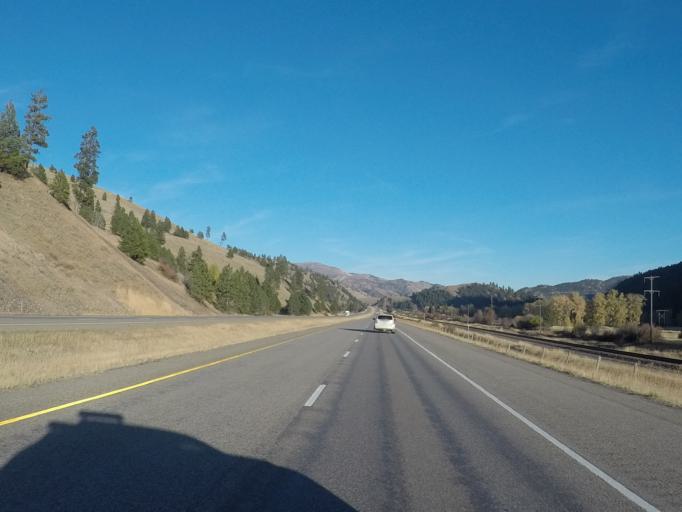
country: US
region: Montana
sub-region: Missoula County
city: Clinton
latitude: 46.7253
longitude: -113.6201
